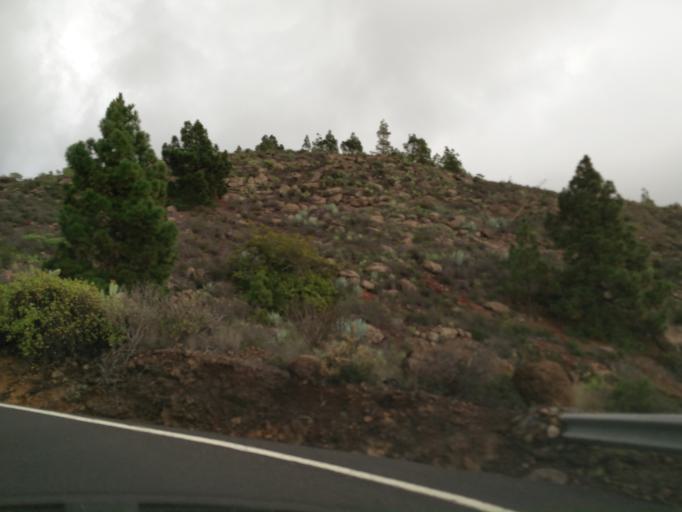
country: ES
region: Canary Islands
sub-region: Provincia de Santa Cruz de Tenerife
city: Arona
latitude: 28.1160
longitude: -16.6776
